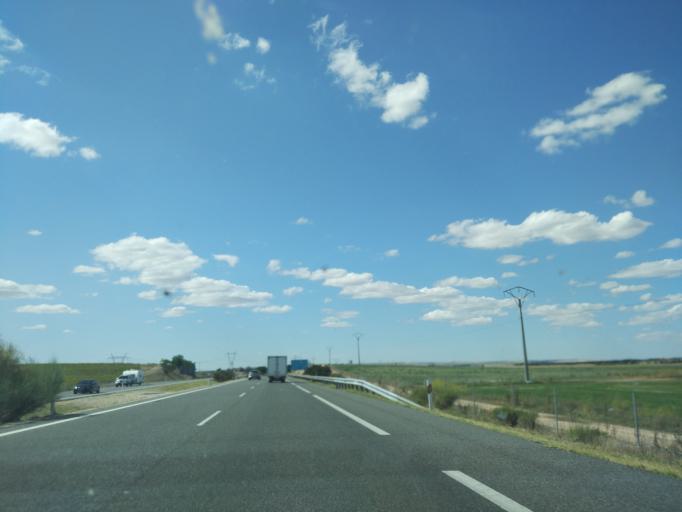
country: ES
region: Castille and Leon
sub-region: Provincia de Valladolid
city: San Vicente del Palacio
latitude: 41.2299
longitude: -4.8519
